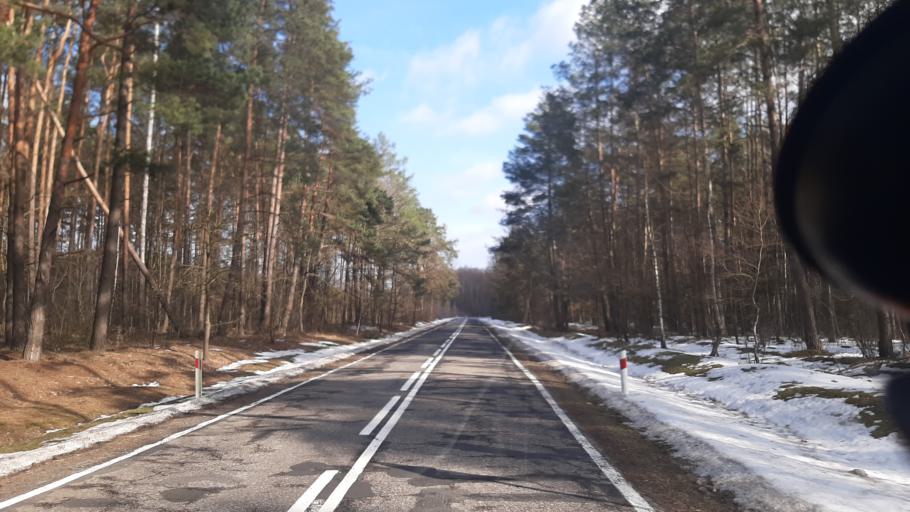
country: PL
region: Lublin Voivodeship
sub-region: Powiat parczewski
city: Sosnowica
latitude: 51.4971
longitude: 23.1838
